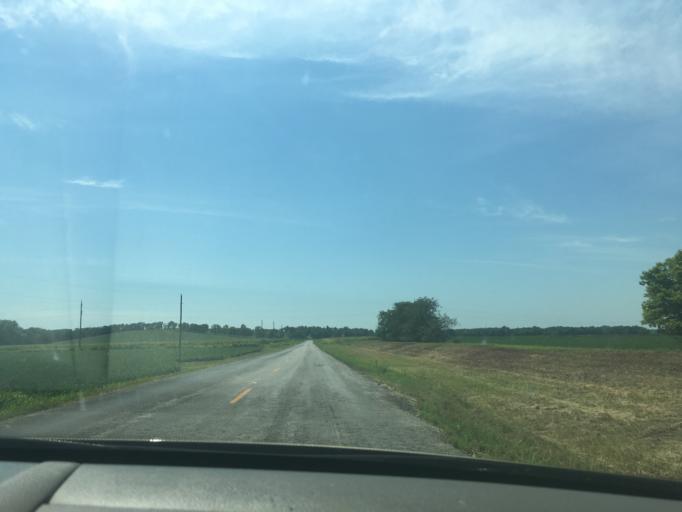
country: US
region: Missouri
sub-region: Gentry County
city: Stanberry
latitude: 40.2371
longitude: -94.7107
